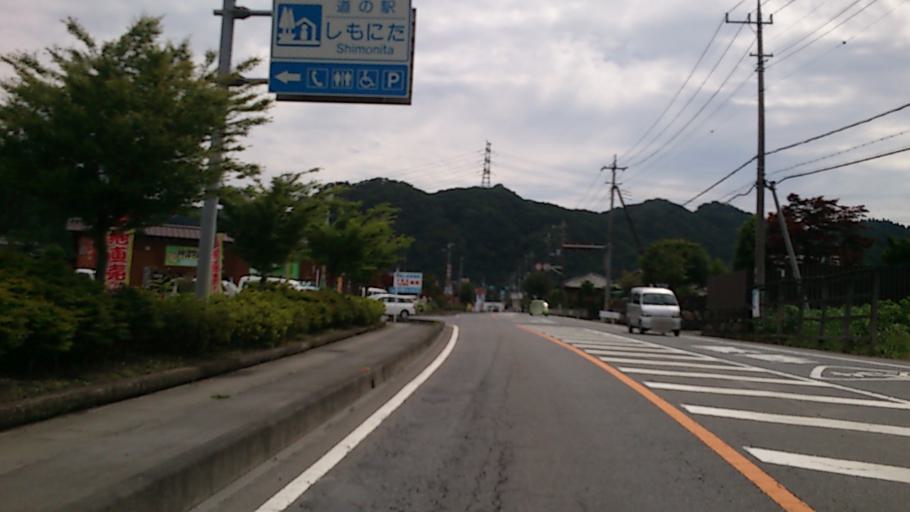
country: JP
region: Gunma
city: Tomioka
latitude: 36.2243
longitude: 138.8020
